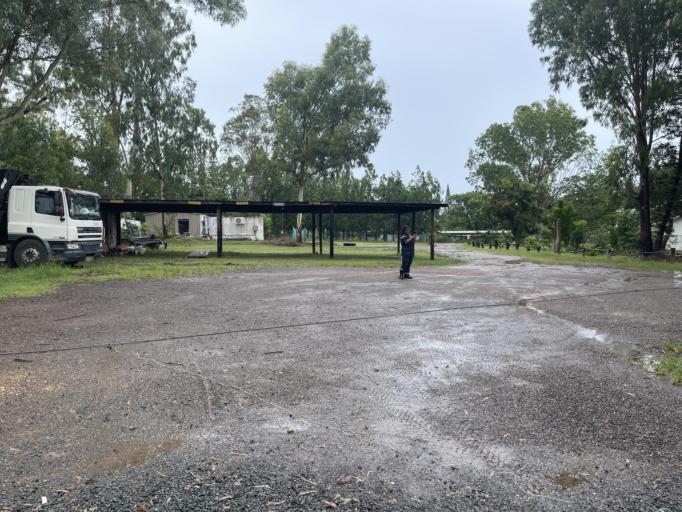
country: NC
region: North Province
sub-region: Koumac
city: Koumac
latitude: -20.5549
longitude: 164.2896
